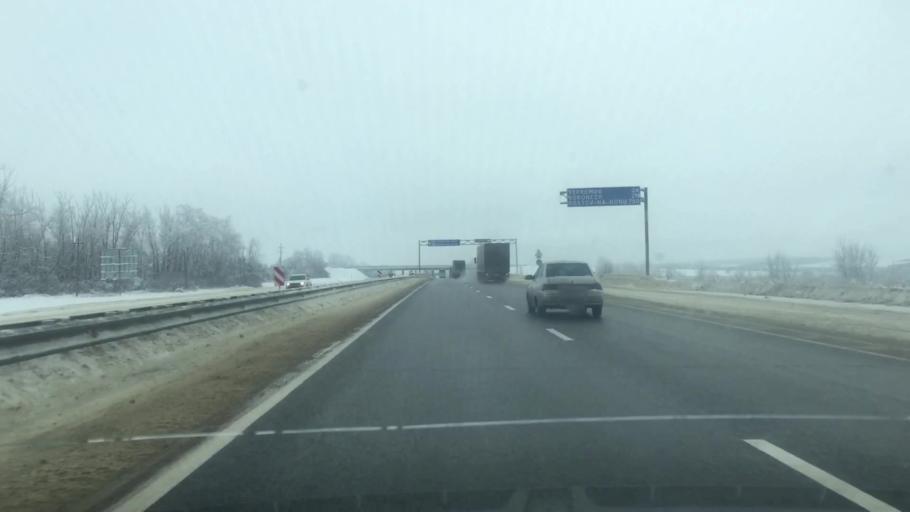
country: RU
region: Tula
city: Kazachka
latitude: 53.3037
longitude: 38.1783
